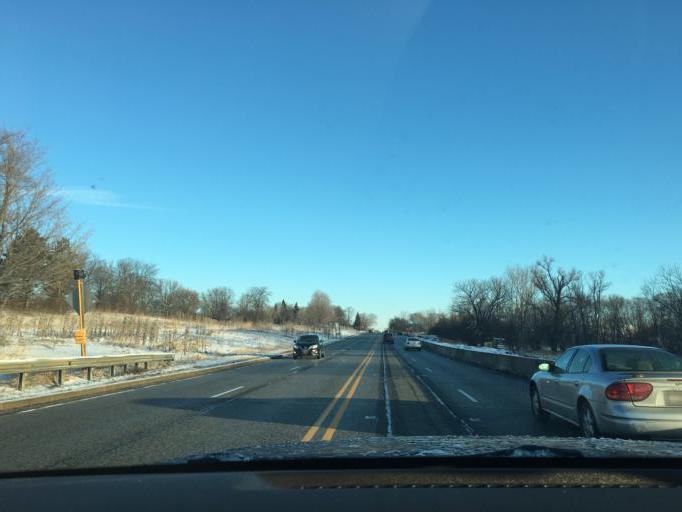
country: US
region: Illinois
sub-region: Cook County
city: Hoffman Estates
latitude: 42.0691
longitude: -88.0779
